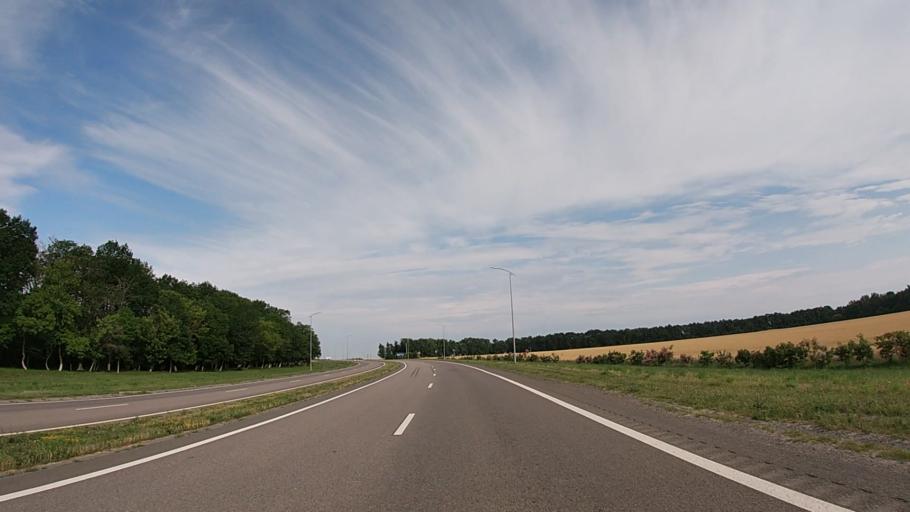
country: RU
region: Belgorod
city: Rakitnoye
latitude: 50.7613
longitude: 35.9620
